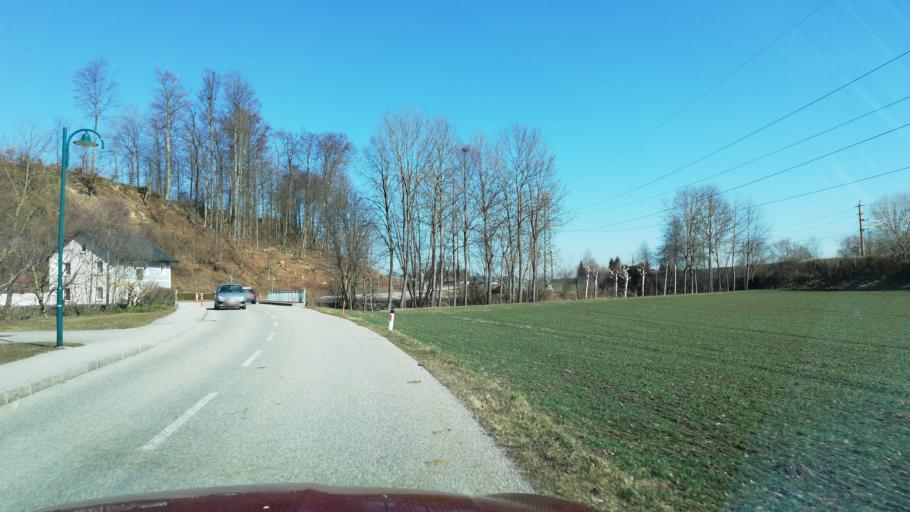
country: AT
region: Upper Austria
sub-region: Politischer Bezirk Vocklabruck
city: Redlham
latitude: 48.0355
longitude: 13.7414
